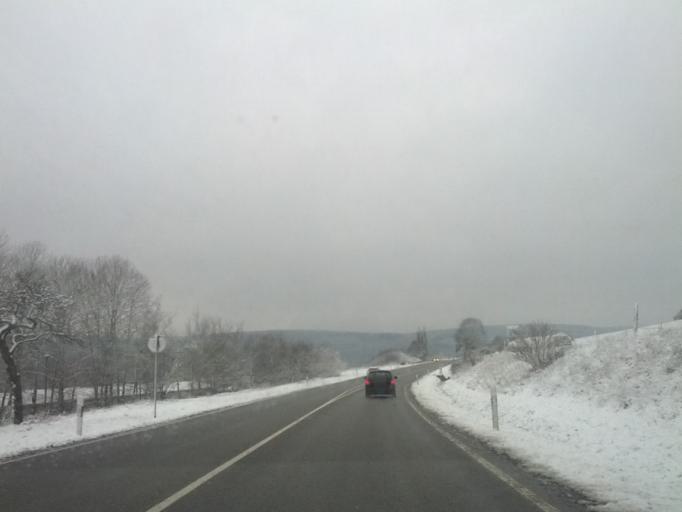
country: DE
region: Thuringia
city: Walldorf
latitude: 50.6214
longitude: 10.3843
